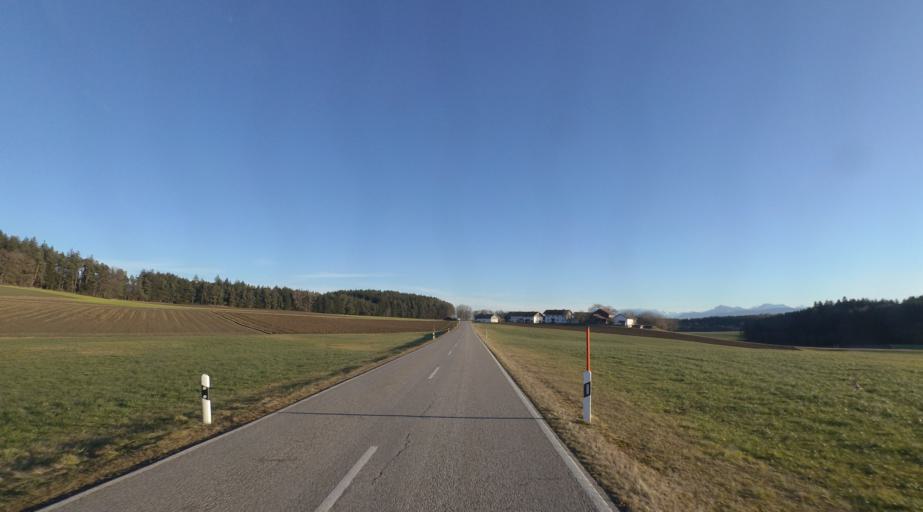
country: DE
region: Bavaria
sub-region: Upper Bavaria
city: Taching am See
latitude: 48.0014
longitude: 12.6955
